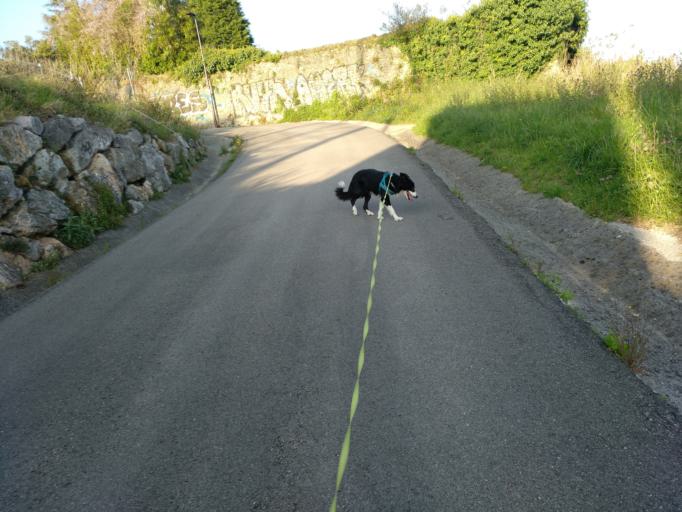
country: ES
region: Asturias
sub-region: Province of Asturias
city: Gijon
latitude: 43.5145
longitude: -5.6644
